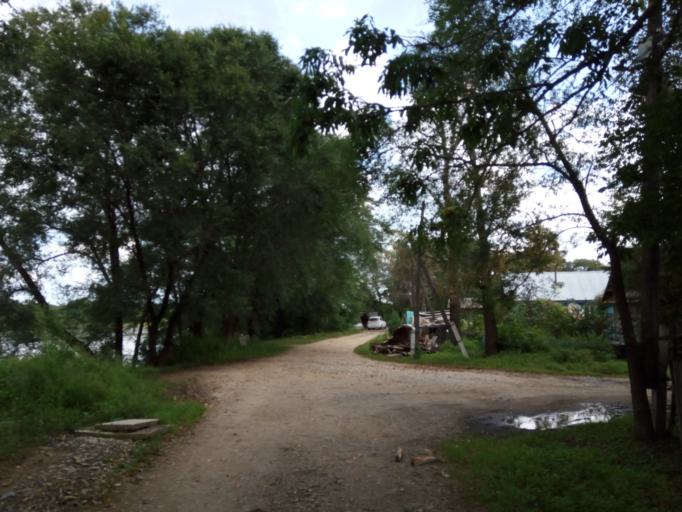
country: RU
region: Primorskiy
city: Dal'nerechensk
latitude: 45.9568
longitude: 133.8191
